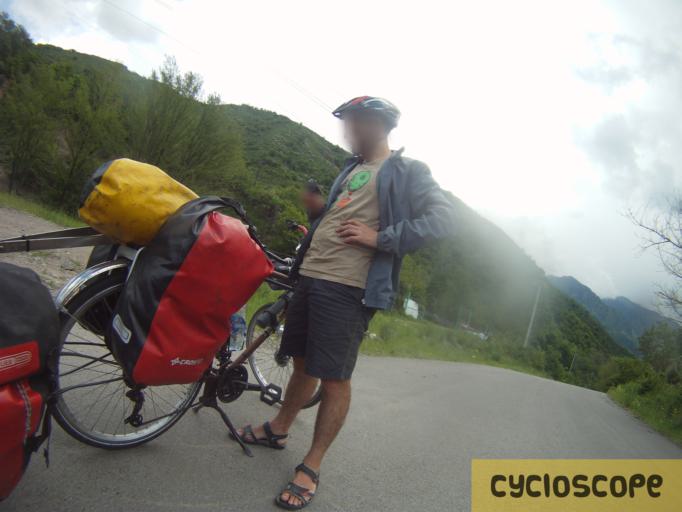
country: KZ
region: Almaty Oblysy
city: Esik
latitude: 43.2987
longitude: 77.5001
